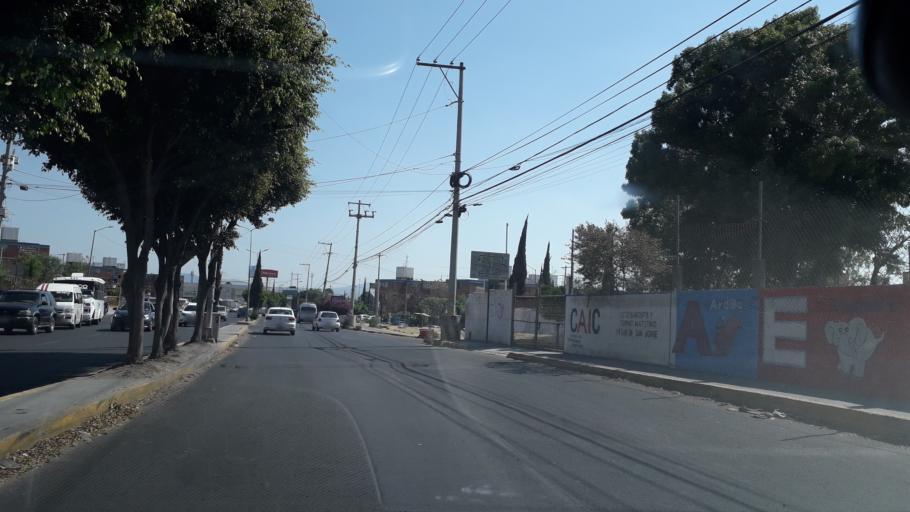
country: MX
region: Puebla
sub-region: Puebla
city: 18 de Marzo
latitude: 18.9853
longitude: -98.2171
